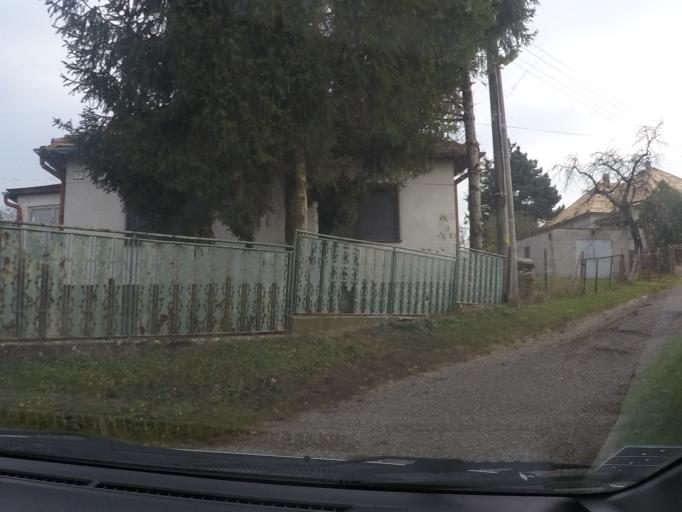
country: SK
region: Nitriansky
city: Svodin
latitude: 48.0419
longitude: 18.4765
